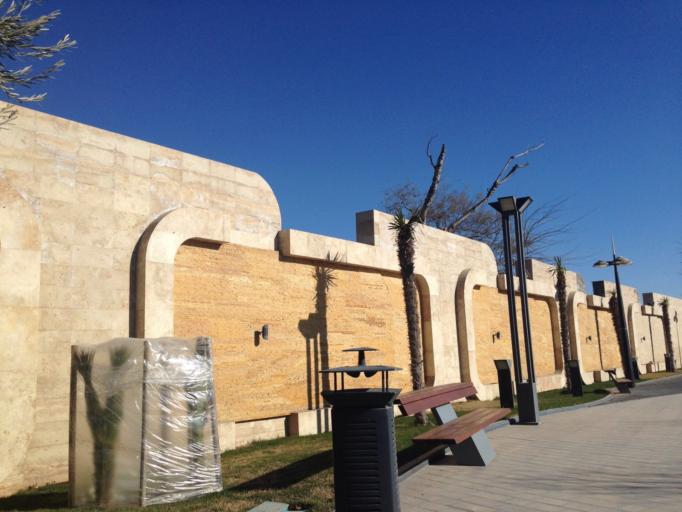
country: AZ
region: Baki
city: Baku
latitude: 40.3752
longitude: 49.8647
